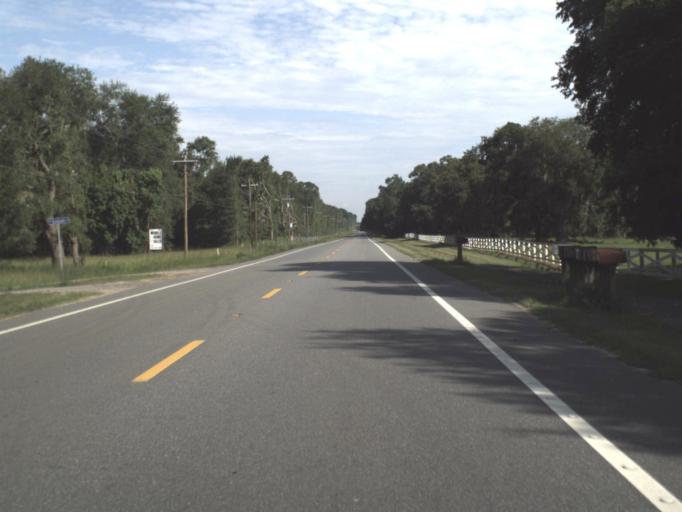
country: US
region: Florida
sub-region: Madison County
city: Madison
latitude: 30.4336
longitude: -83.3903
